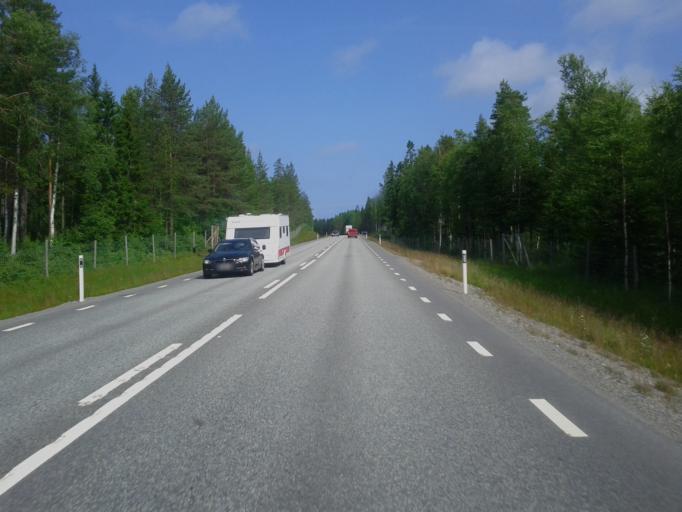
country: SE
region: Vaesterbotten
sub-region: Skelleftea Kommun
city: Burea
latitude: 64.5317
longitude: 21.2588
